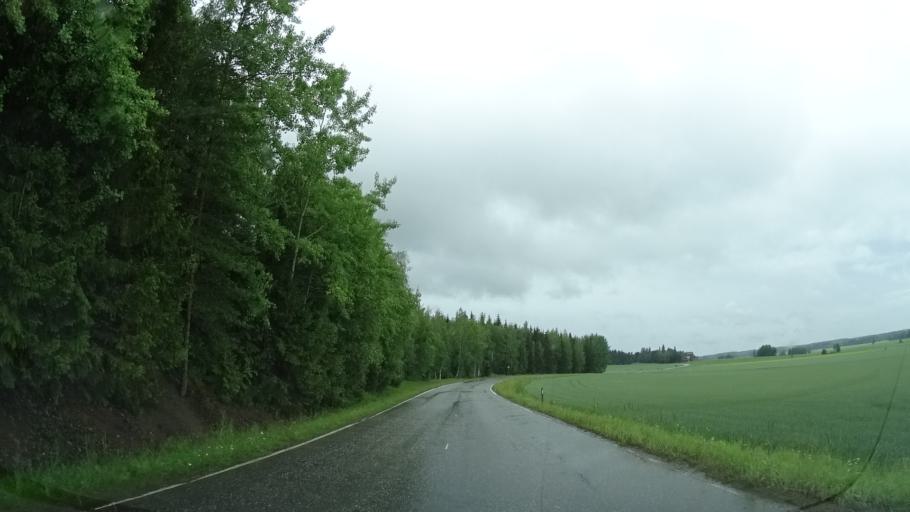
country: FI
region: Haeme
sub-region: Forssa
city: Humppila
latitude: 61.0072
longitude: 23.2546
